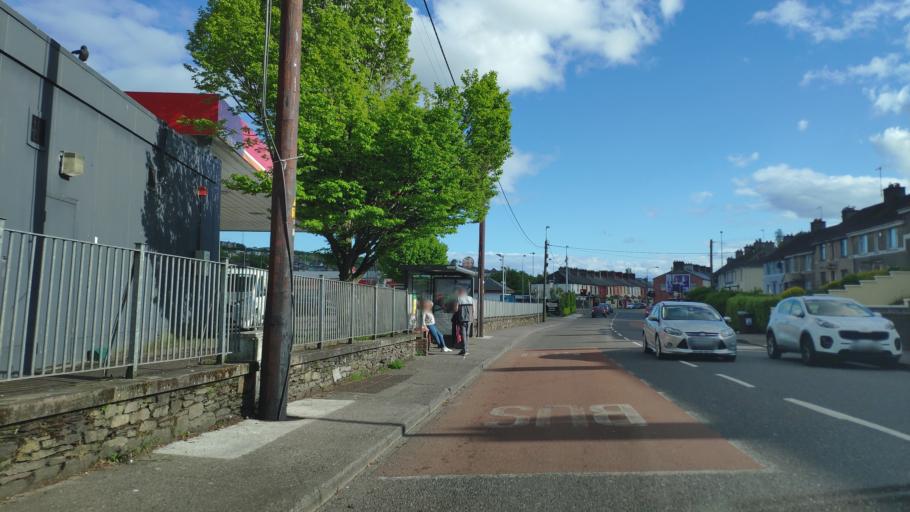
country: IE
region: Munster
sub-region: County Cork
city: Cork
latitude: 51.9165
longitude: -8.4744
